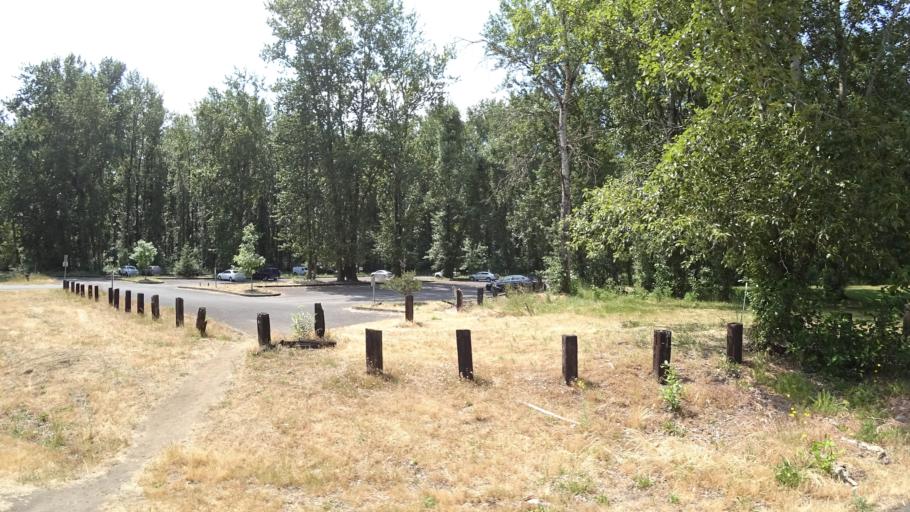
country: US
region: Washington
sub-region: Clark County
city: Felida
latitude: 45.6435
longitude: -122.7648
